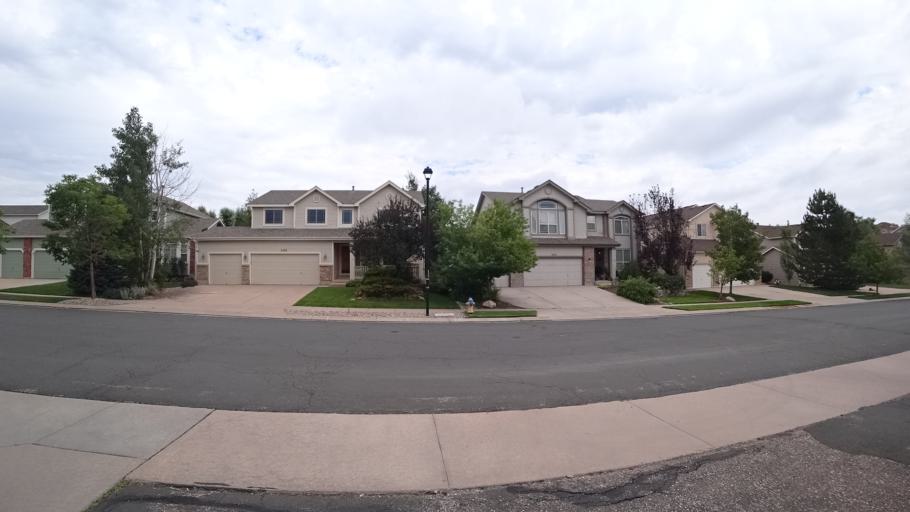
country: US
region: Colorado
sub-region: El Paso County
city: Gleneagle
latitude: 39.0062
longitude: -104.8008
